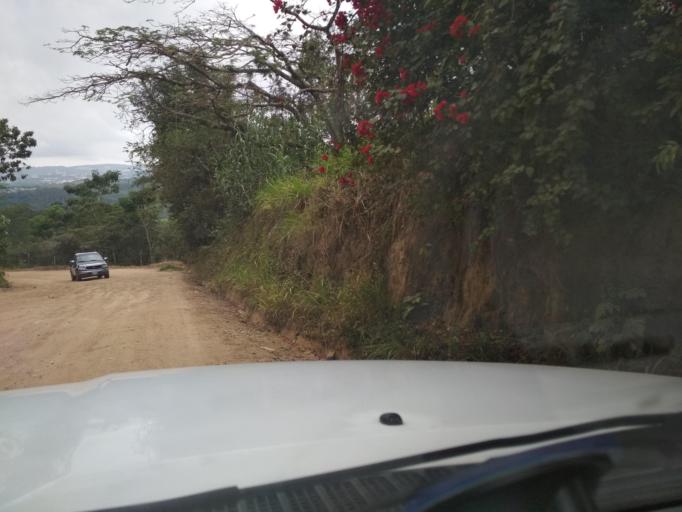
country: MX
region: Veracruz
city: El Castillo
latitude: 19.5454
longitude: -96.8314
